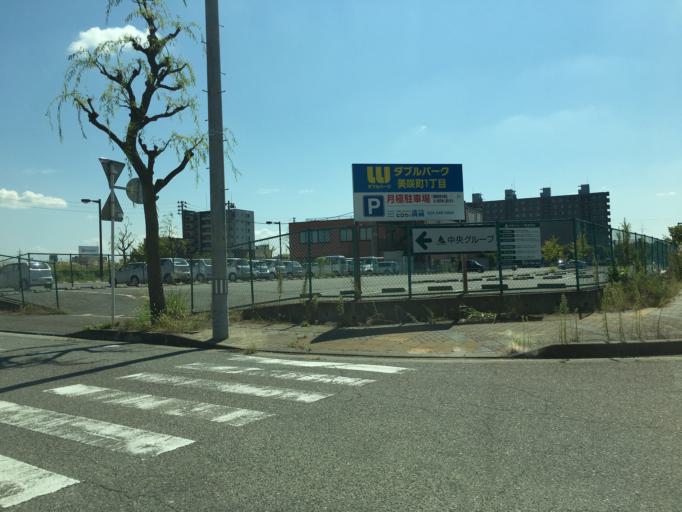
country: JP
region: Niigata
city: Niigata-shi
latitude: 37.8946
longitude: 139.0170
